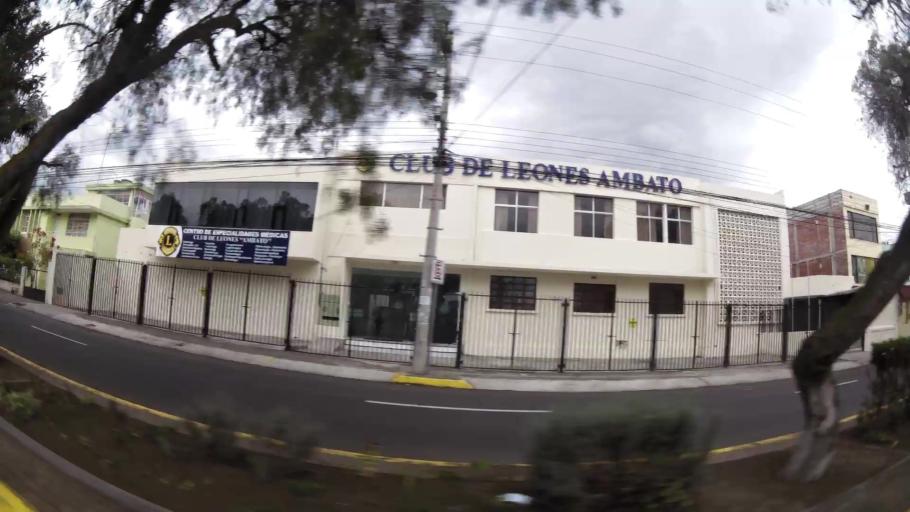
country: EC
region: Tungurahua
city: Ambato
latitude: -1.2318
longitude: -78.6164
